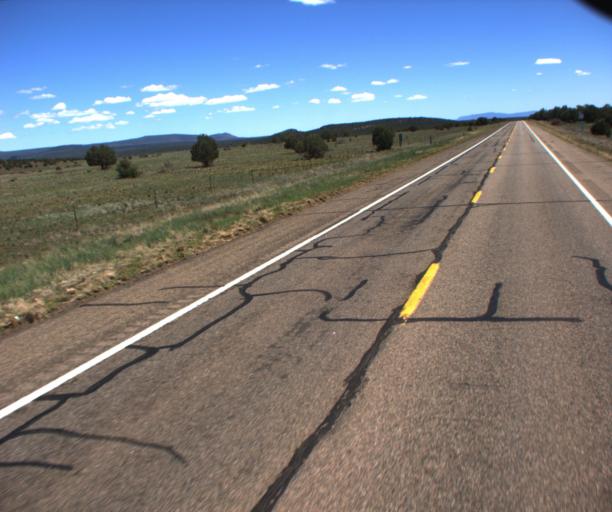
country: US
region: Arizona
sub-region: Yavapai County
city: Paulden
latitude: 35.1554
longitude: -112.4528
